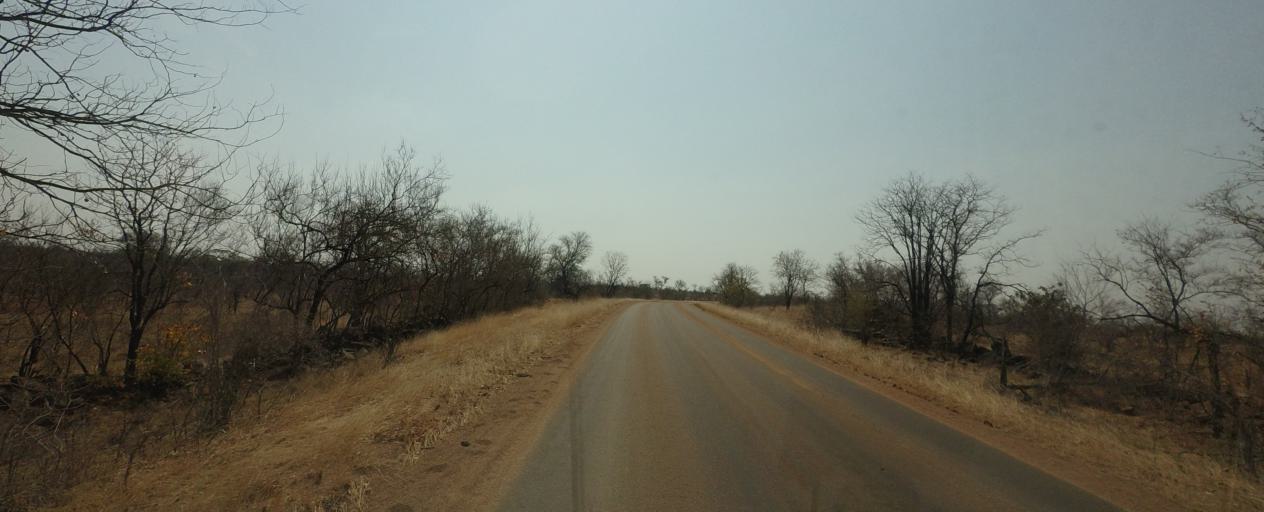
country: ZA
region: Limpopo
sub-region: Mopani District Municipality
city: Giyani
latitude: -23.2089
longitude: 31.3111
